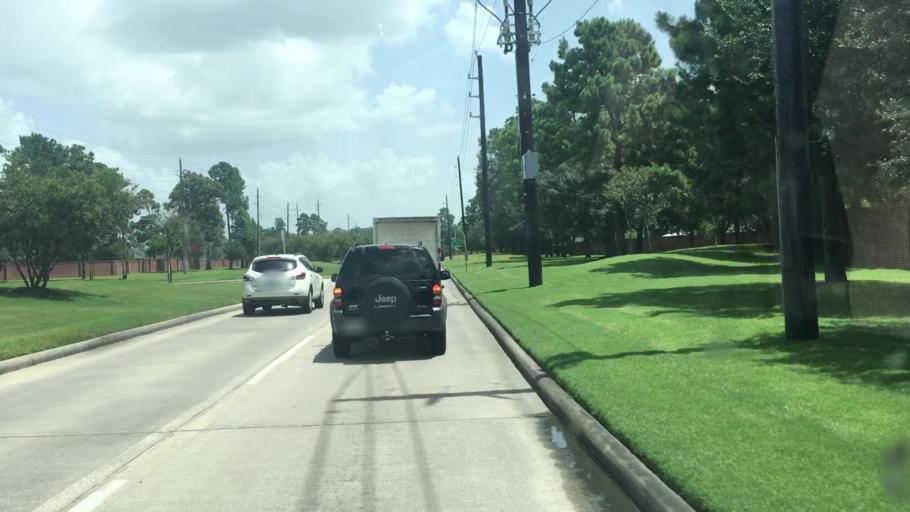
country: US
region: Texas
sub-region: Harris County
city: Atascocita
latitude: 29.9548
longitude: -95.1729
